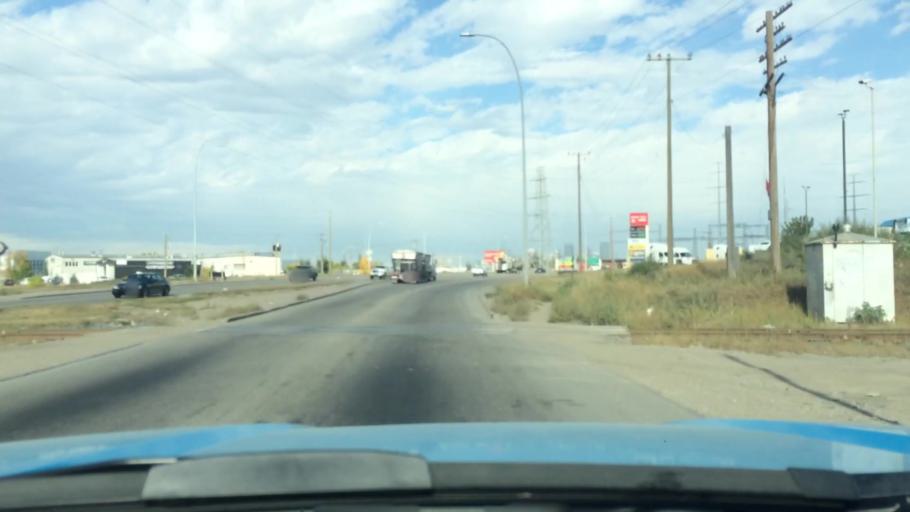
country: CA
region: Alberta
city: Calgary
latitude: 51.0067
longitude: -113.9993
